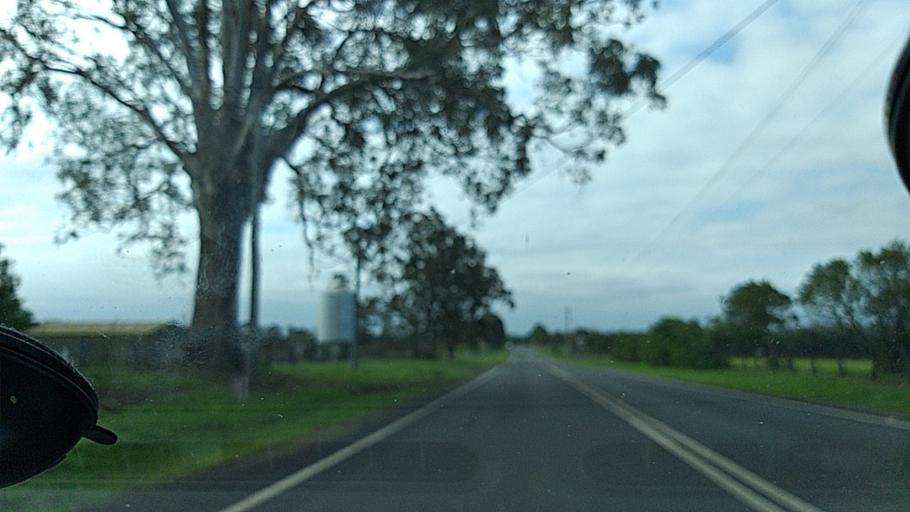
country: AU
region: New South Wales
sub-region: Campbelltown Municipality
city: Glen Alpine
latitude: -34.1236
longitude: 150.7389
